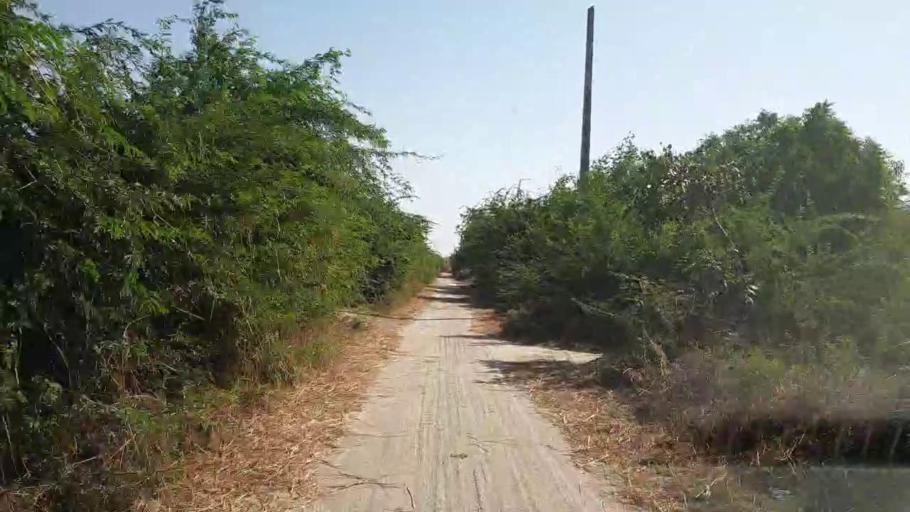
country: PK
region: Sindh
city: Tando Bago
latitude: 24.6383
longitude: 68.9908
